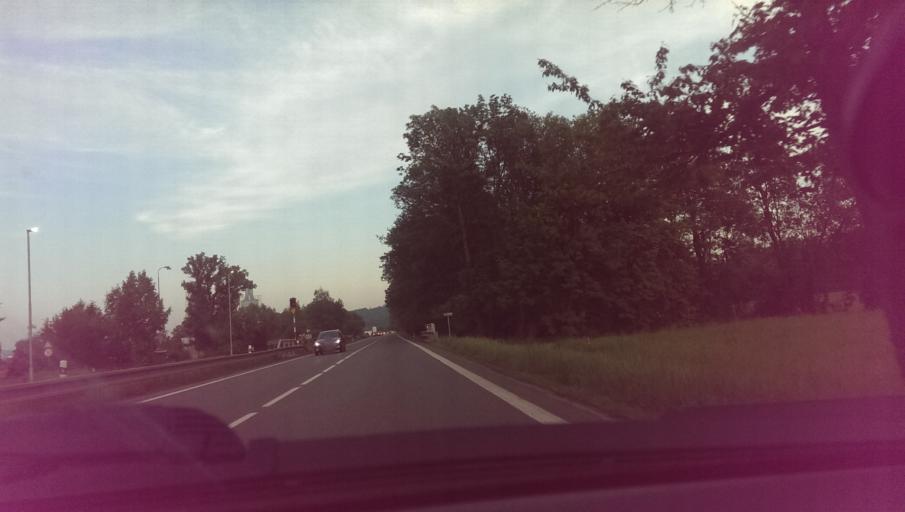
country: CZ
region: Zlin
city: Zasova
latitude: 49.4649
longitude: 18.0652
